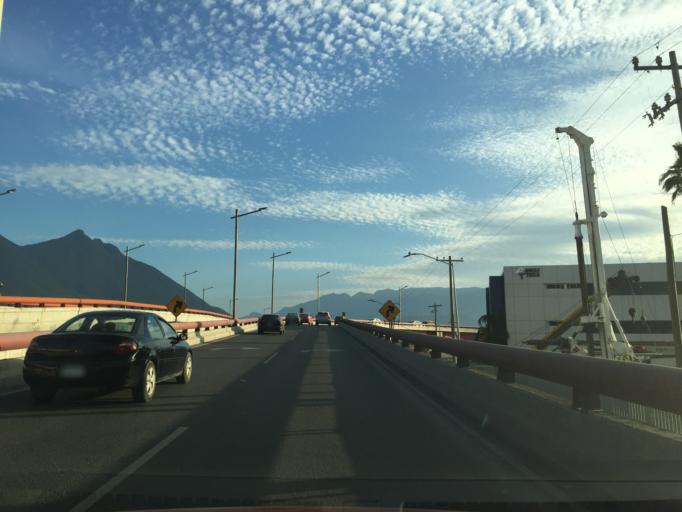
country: MX
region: Nuevo Leon
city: Guadalupe
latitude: 25.6840
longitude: -100.2685
